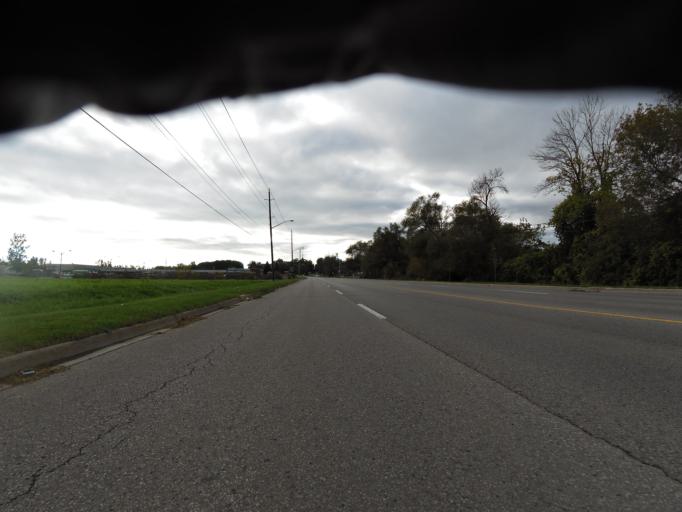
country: CA
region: Ontario
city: Cobourg
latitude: 43.9548
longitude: -78.2698
